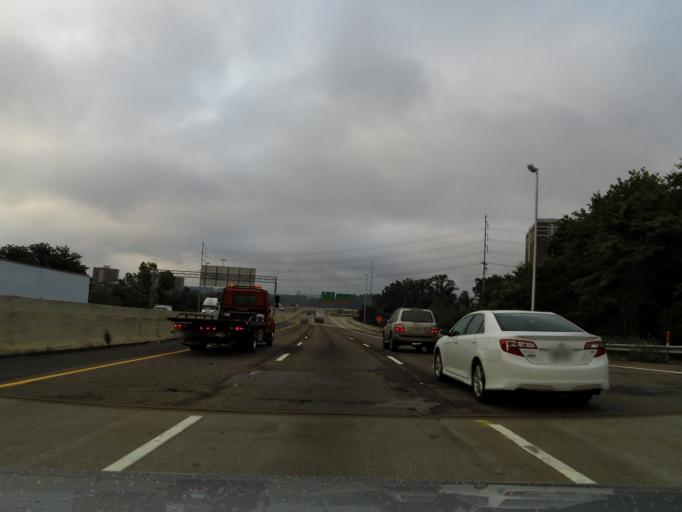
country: US
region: Tennessee
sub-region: Knox County
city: Knoxville
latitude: 35.9558
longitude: -83.9455
